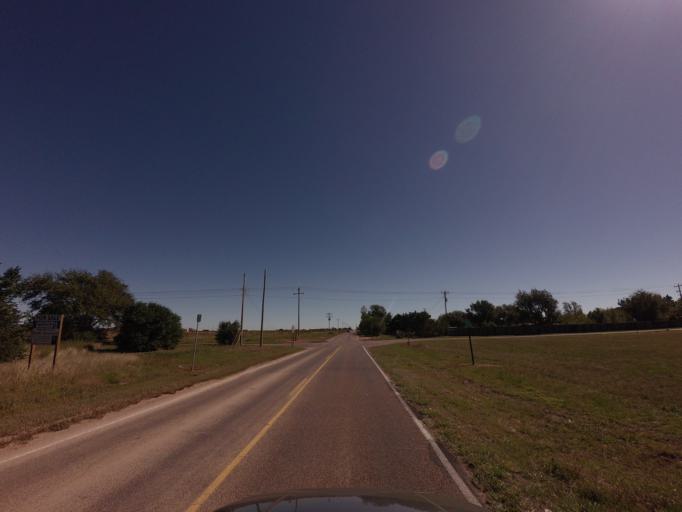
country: US
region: New Mexico
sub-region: Curry County
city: Clovis
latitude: 34.4194
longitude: -103.1614
